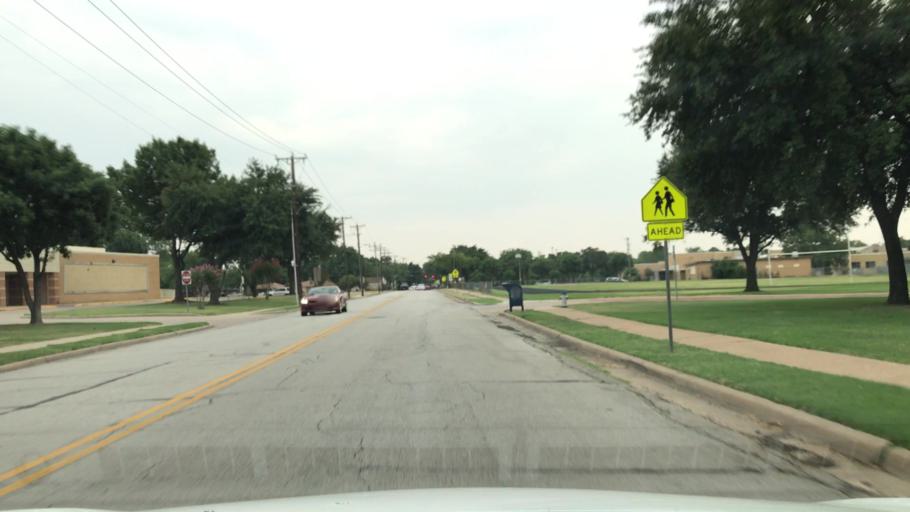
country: US
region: Texas
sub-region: Dallas County
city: Carrollton
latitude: 32.9572
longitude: -96.8955
